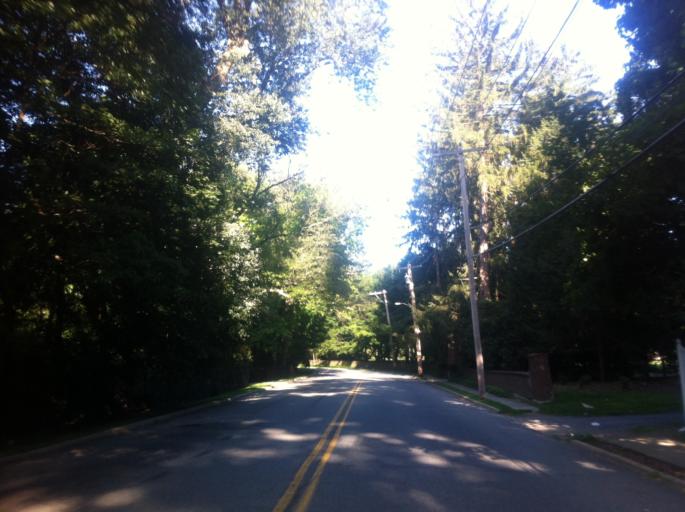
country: US
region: New York
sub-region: Nassau County
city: Locust Valley
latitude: 40.8828
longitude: -73.5927
